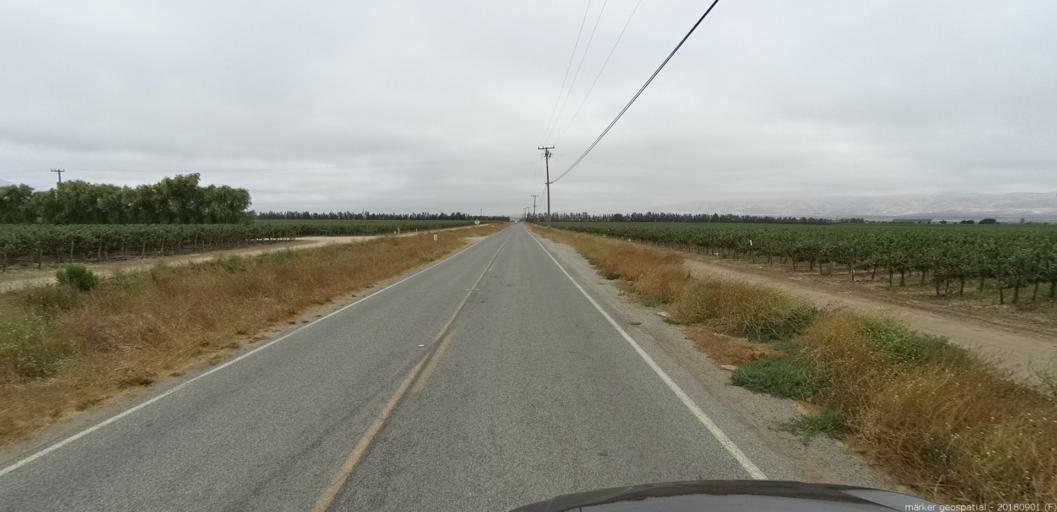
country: US
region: California
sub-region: Monterey County
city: Soledad
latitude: 36.3610
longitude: -121.3208
